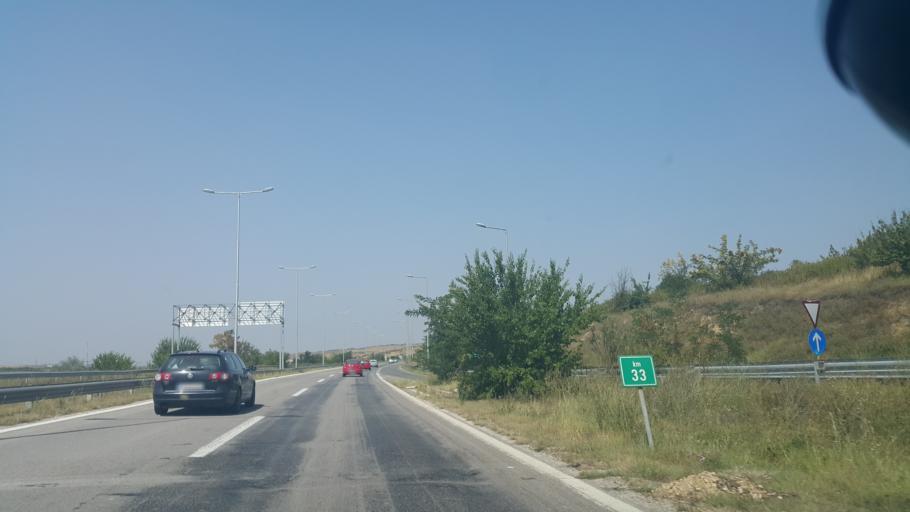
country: MK
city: Miladinovci
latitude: 41.9612
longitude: 21.6340
